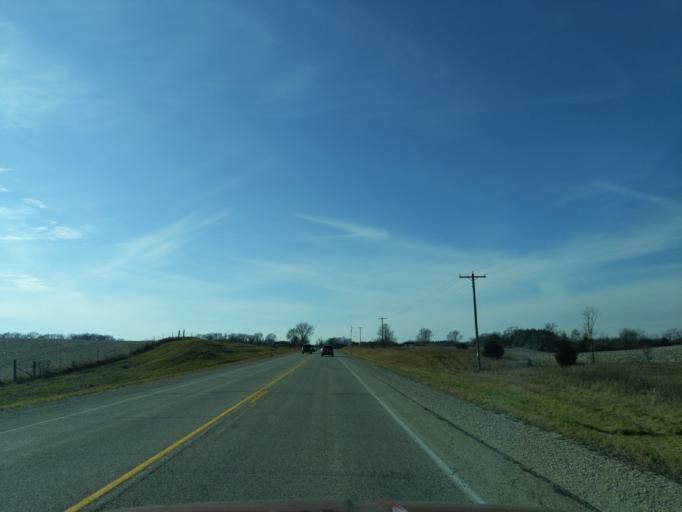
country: US
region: Wisconsin
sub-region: Rock County
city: Milton
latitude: 42.8291
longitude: -88.8746
